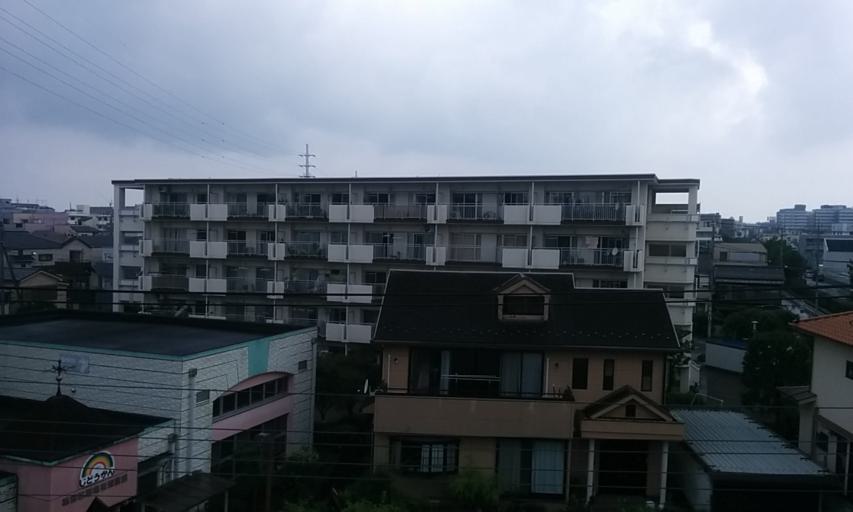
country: JP
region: Saitama
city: Yashio-shi
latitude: 35.7648
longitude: 139.8440
